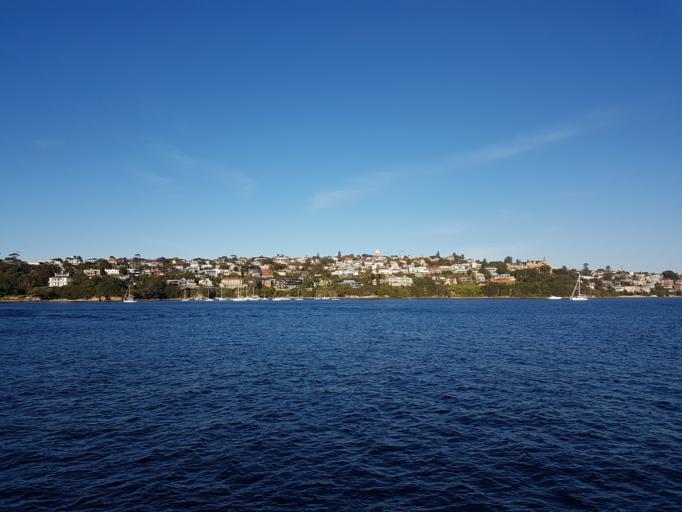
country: AU
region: New South Wales
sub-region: Woollahra
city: Point Piper
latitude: -33.8577
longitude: 151.2612
